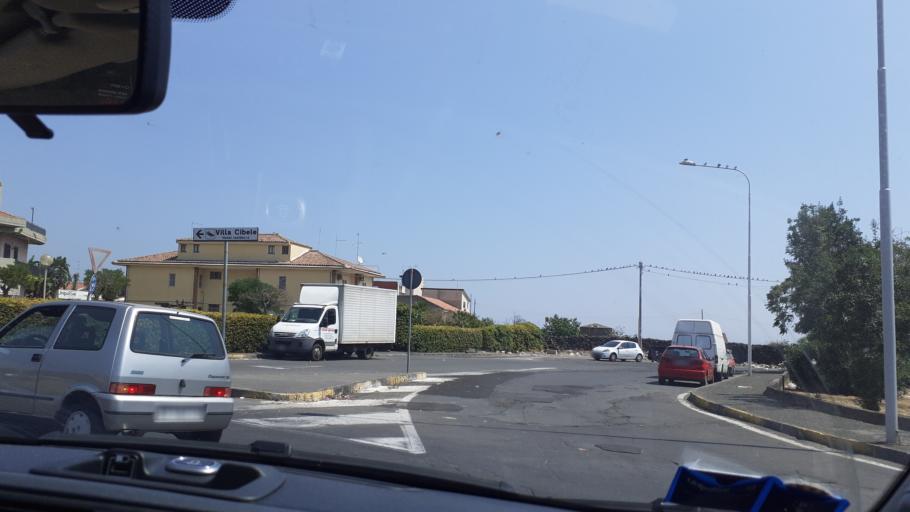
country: IT
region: Sicily
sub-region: Catania
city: Catania
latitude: 37.5133
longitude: 15.0563
